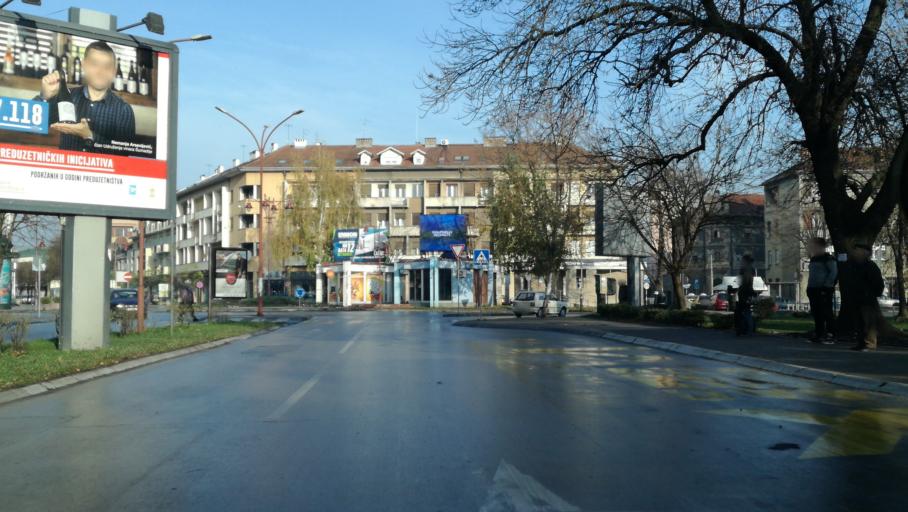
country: RS
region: Central Serbia
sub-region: Moravicki Okrug
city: Cacak
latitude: 43.8897
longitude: 20.3527
